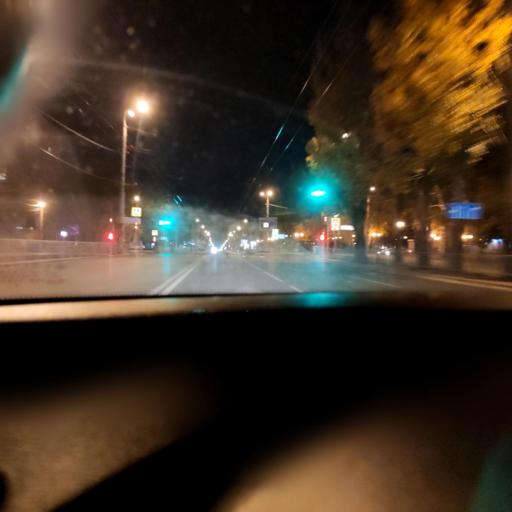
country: RU
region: Samara
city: Samara
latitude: 53.2354
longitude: 50.2215
